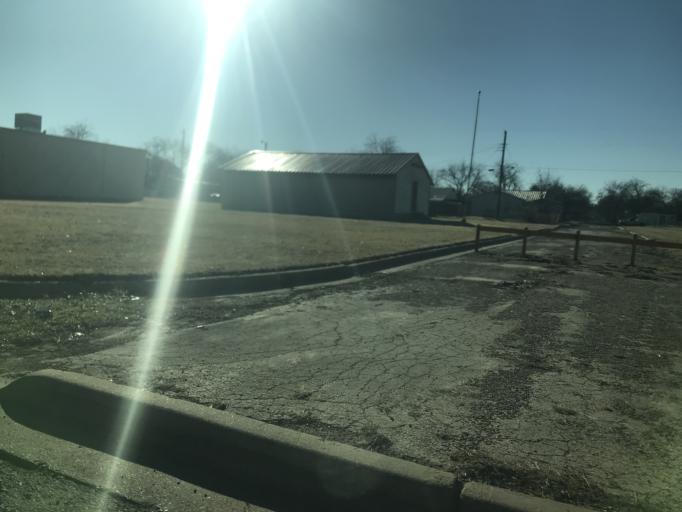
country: US
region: Texas
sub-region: Taylor County
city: Abilene
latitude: 32.4395
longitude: -99.7586
